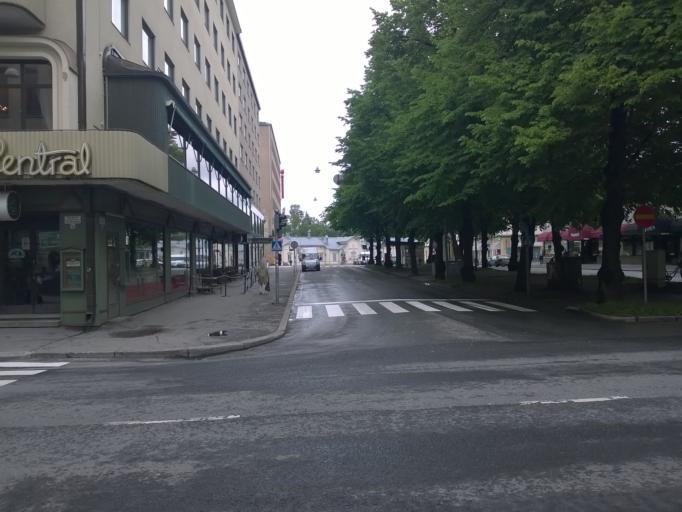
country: FI
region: Ostrobothnia
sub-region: Vaasa
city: Vaasa
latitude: 63.0970
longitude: 21.6182
